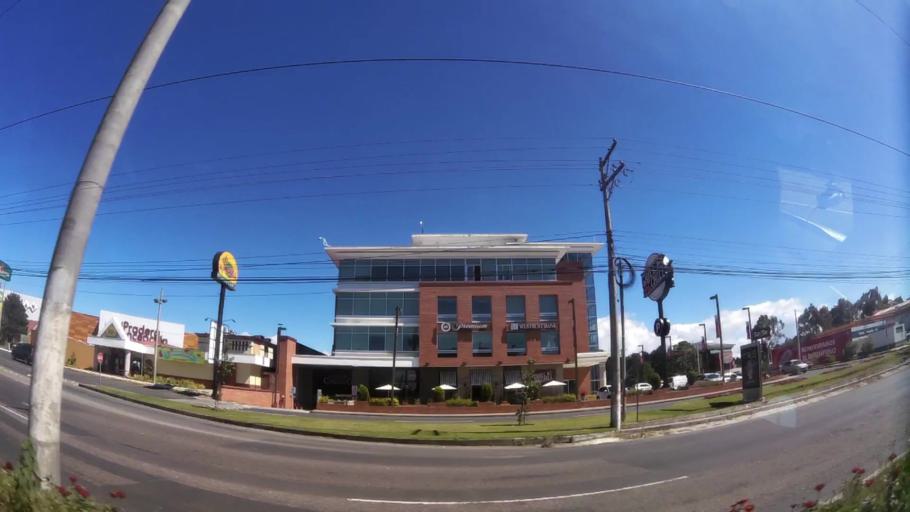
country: GT
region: Guatemala
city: San Jose Pinula
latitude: 14.5499
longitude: -90.4549
